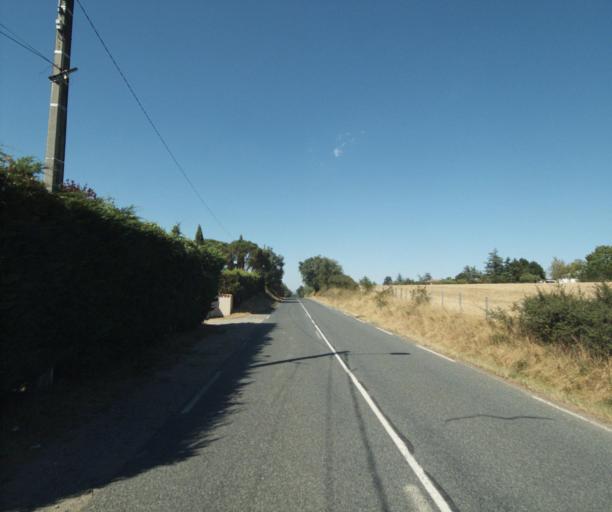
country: FR
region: Rhone-Alpes
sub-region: Departement du Rhone
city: La Tour-de-Salvagny
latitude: 45.8290
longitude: 4.6969
